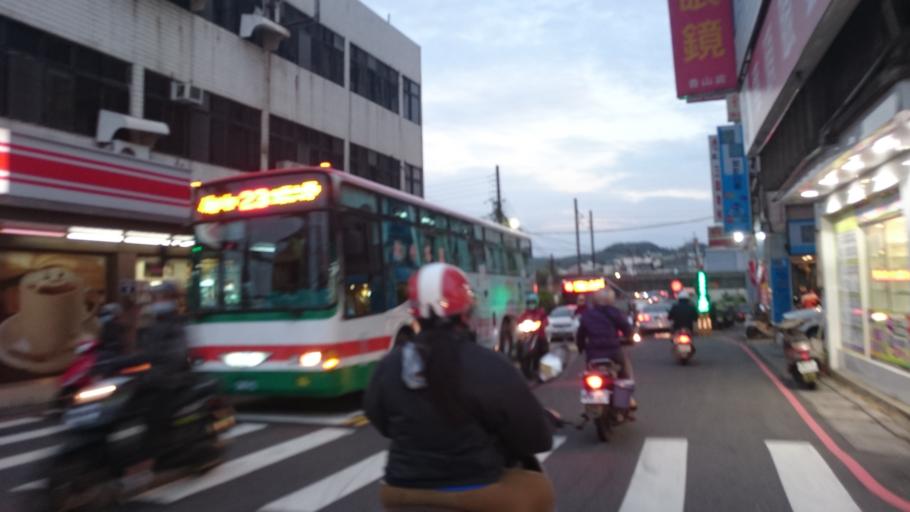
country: TW
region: Taiwan
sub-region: Hsinchu
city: Hsinchu
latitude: 24.7882
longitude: 120.9287
